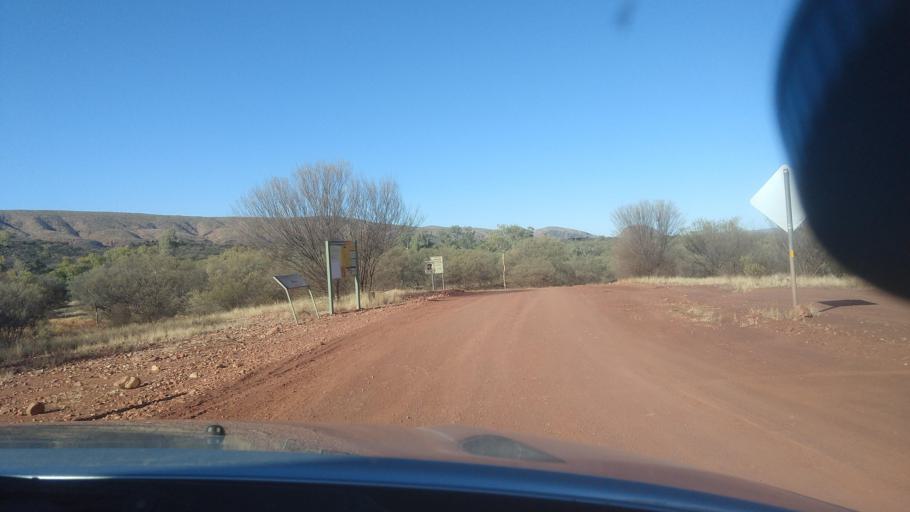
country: AU
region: Northern Territory
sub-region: Alice Springs
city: Alice Springs
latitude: -23.7536
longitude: 132.9177
